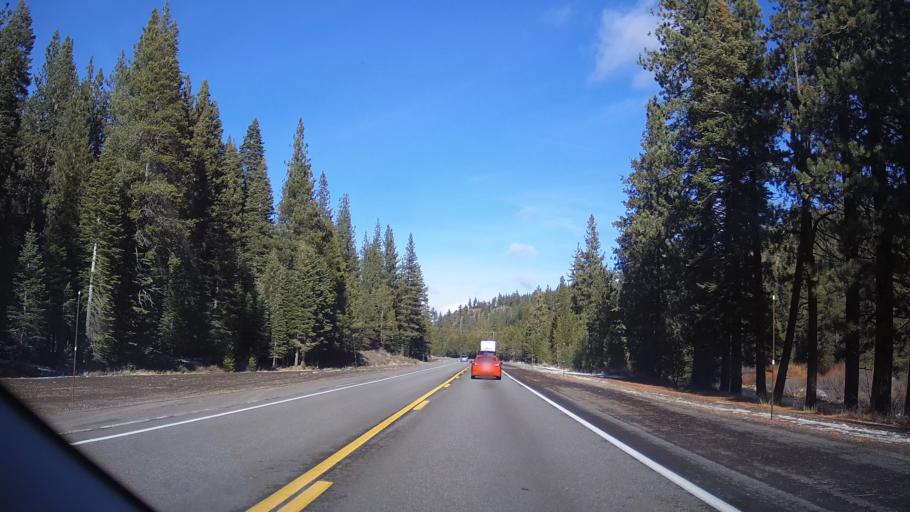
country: US
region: California
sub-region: Nevada County
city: Truckee
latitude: 39.2697
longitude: -120.2079
